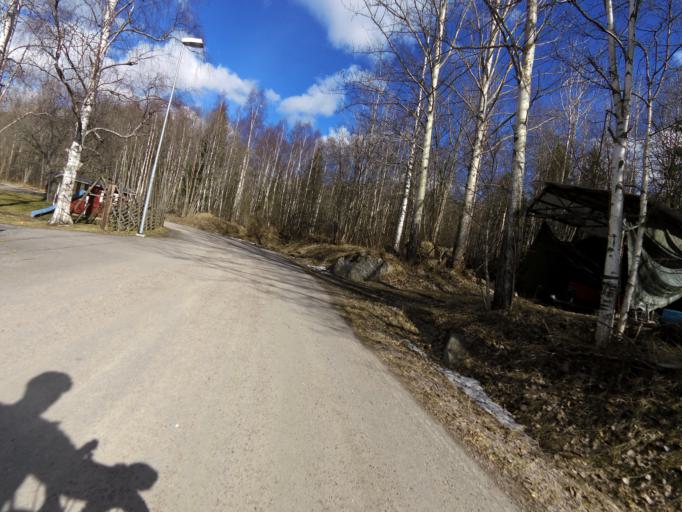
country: SE
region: Gaevleborg
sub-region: Hofors Kommun
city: Hofors
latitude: 60.5424
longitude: 16.3121
